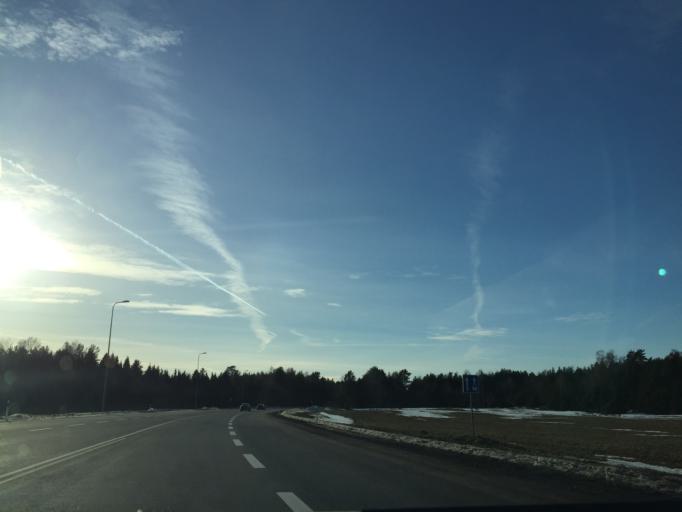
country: EE
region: Saare
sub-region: Kuressaare linn
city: Kuressaare
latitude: 58.3533
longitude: 22.7039
